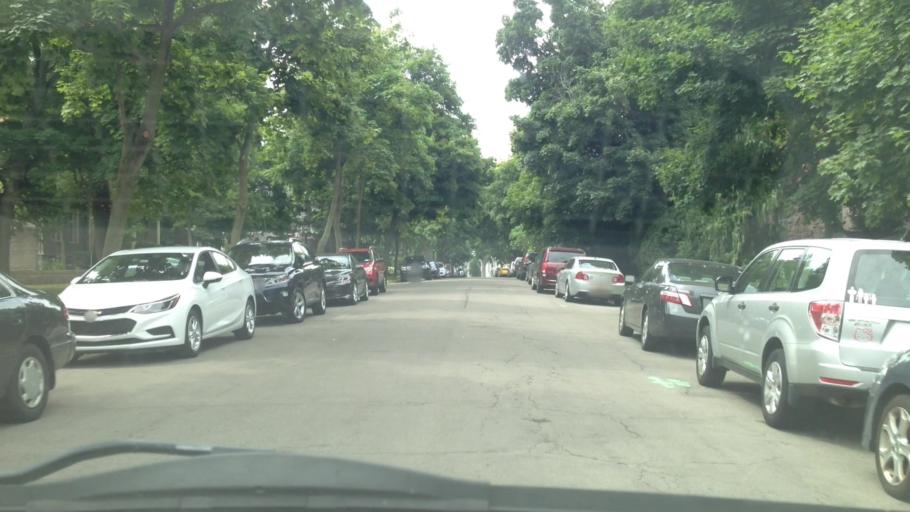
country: US
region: New York
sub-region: Erie County
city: Kenmore
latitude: 42.9358
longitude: -78.8477
